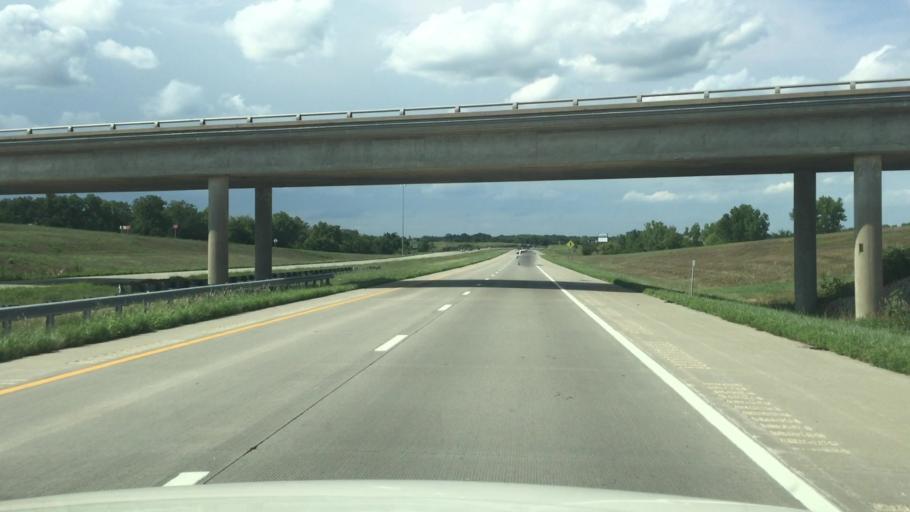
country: US
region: Kansas
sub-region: Miami County
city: Louisburg
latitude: 38.5633
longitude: -94.6934
